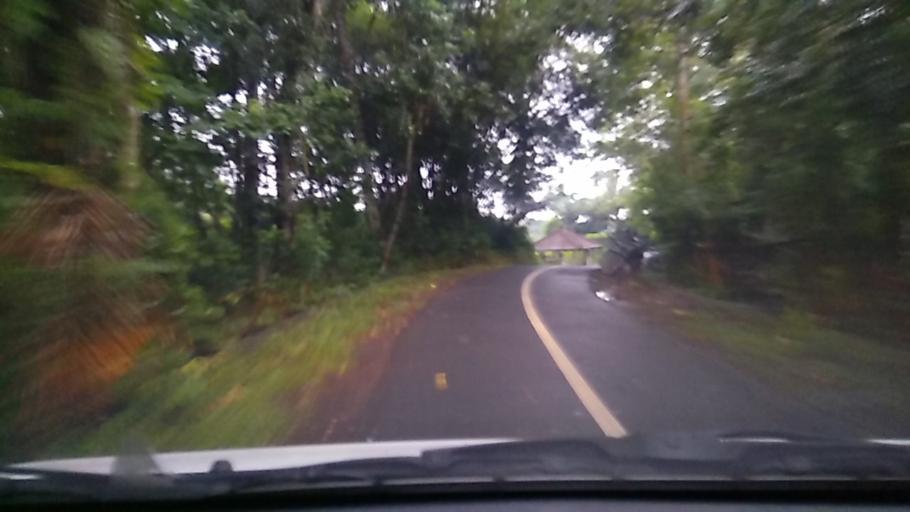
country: ID
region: Bali
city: Tiyingtali Kelod
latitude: -8.4051
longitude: 115.6181
